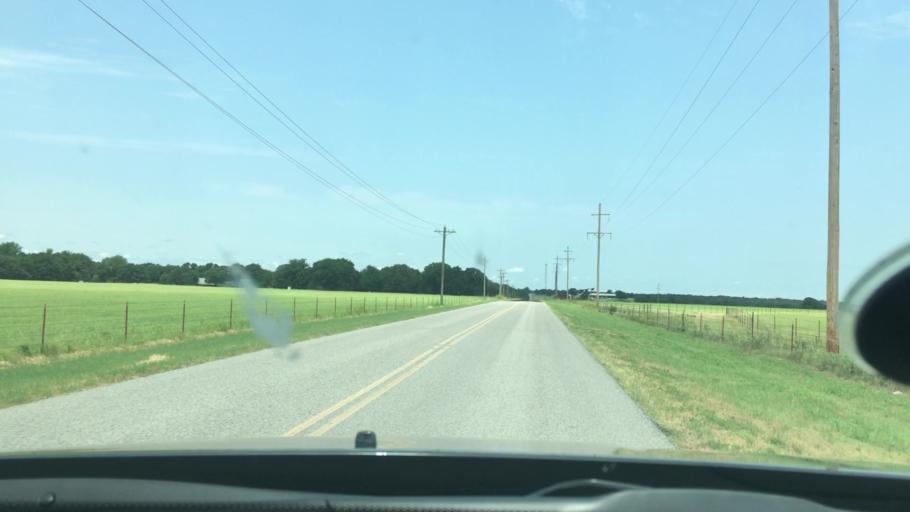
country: US
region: Oklahoma
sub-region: Love County
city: Marietta
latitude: 33.9186
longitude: -97.3521
